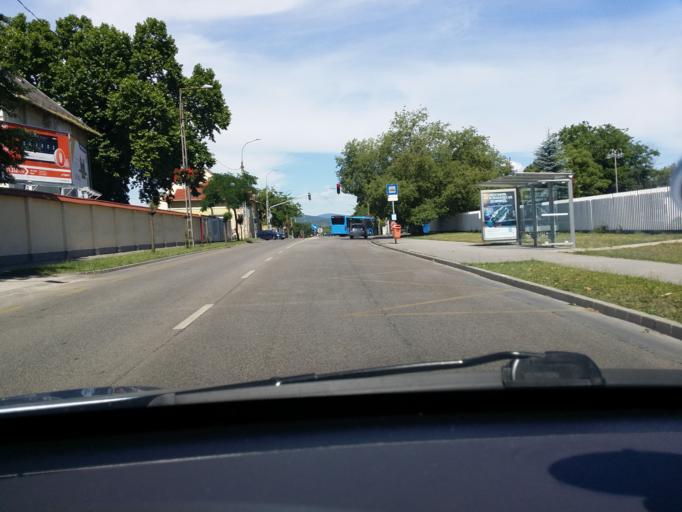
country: HU
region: Budapest
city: Budapest IV. keruelet
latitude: 47.5770
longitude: 19.0942
